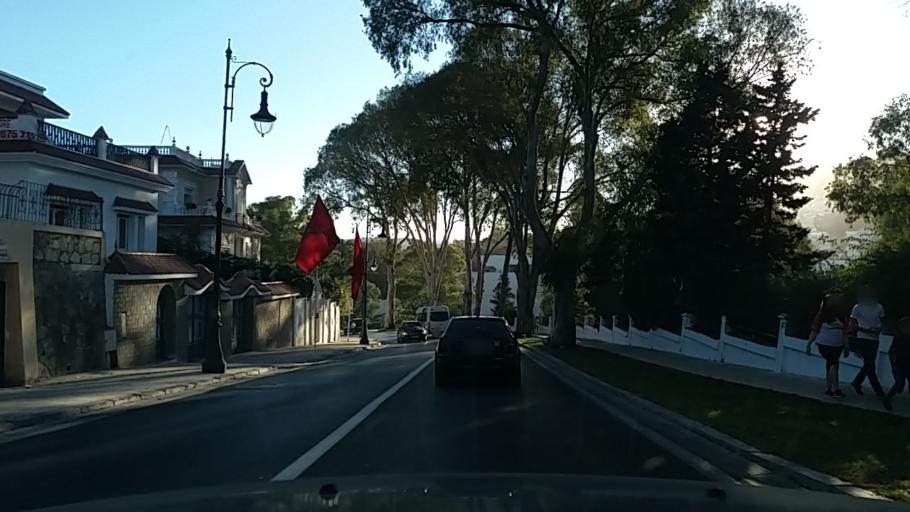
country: MA
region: Tanger-Tetouan
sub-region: Tanger-Assilah
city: Tangier
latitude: 35.7806
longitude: -5.8374
